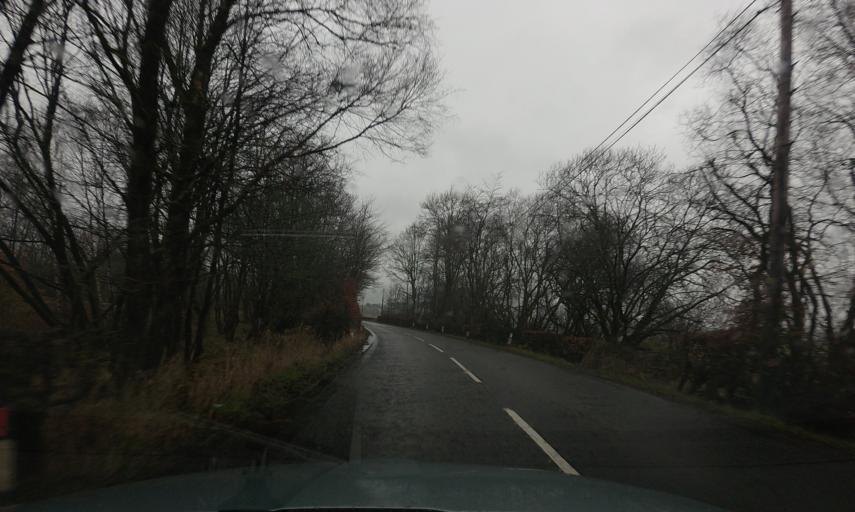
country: GB
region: Scotland
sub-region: Stirling
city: Balfron
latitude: 56.1469
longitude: -4.3600
